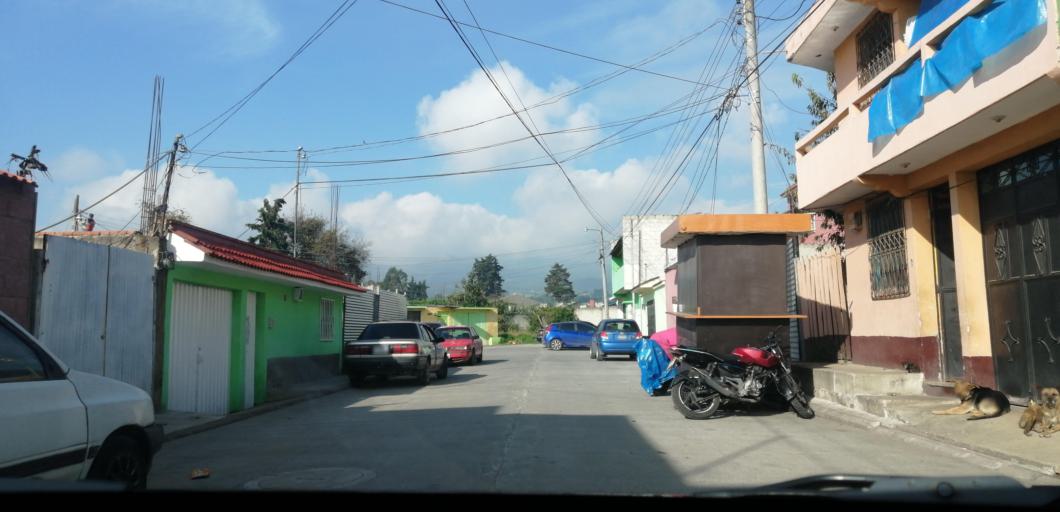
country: GT
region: Quetzaltenango
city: Quetzaltenango
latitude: 14.8587
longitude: -91.5366
